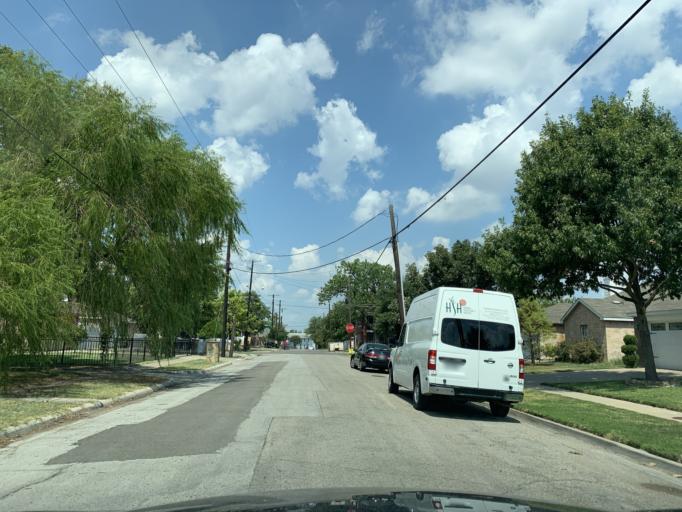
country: US
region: Texas
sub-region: Dallas County
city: Dallas
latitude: 32.7483
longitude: -96.8178
